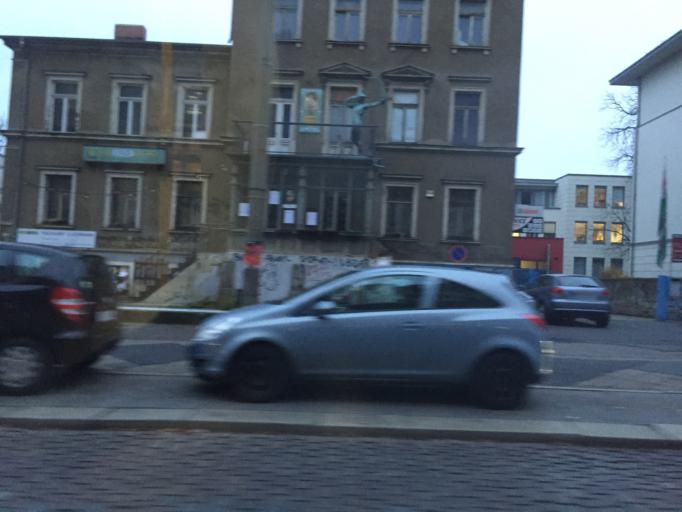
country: DE
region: Saxony
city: Albertstadt
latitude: 51.0701
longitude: 13.7495
